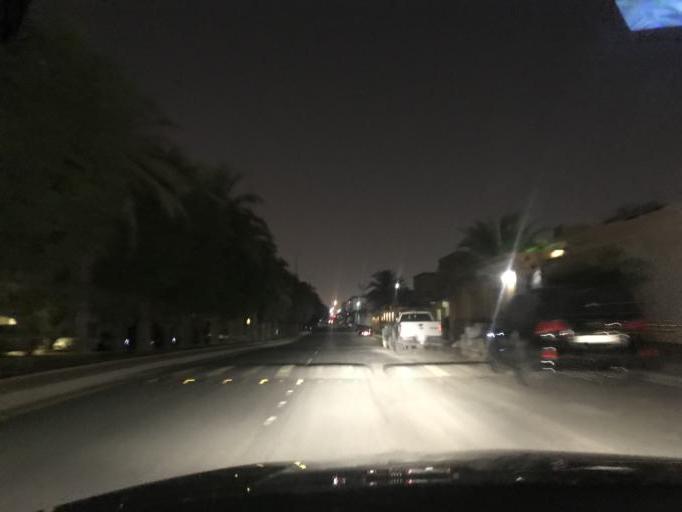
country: SA
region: Ar Riyad
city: Riyadh
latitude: 24.7131
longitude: 46.7780
